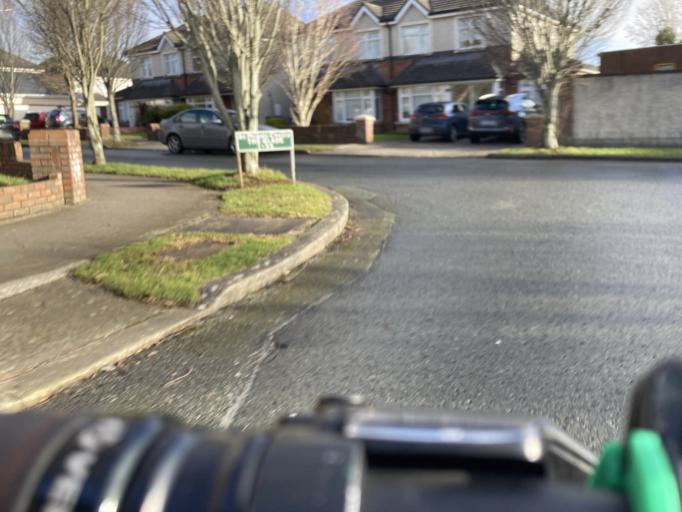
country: IE
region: Leinster
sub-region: Kildare
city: Celbridge
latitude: 53.3458
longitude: -6.5512
